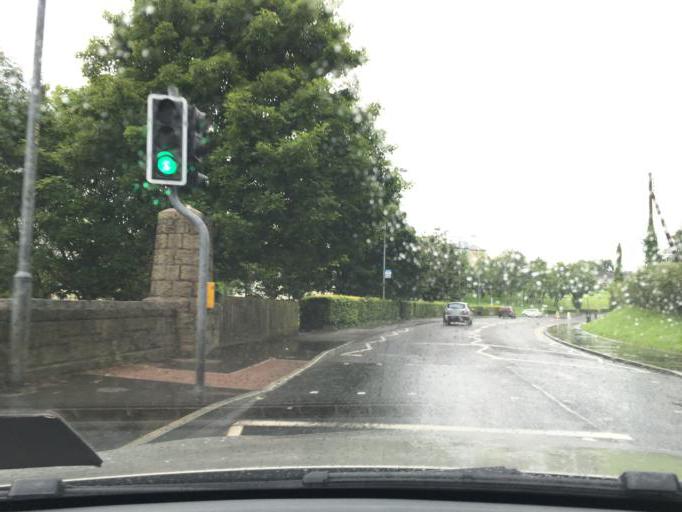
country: GB
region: Northern Ireland
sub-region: Fermanagh District
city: Enniskillen
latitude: 54.3492
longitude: -7.6396
